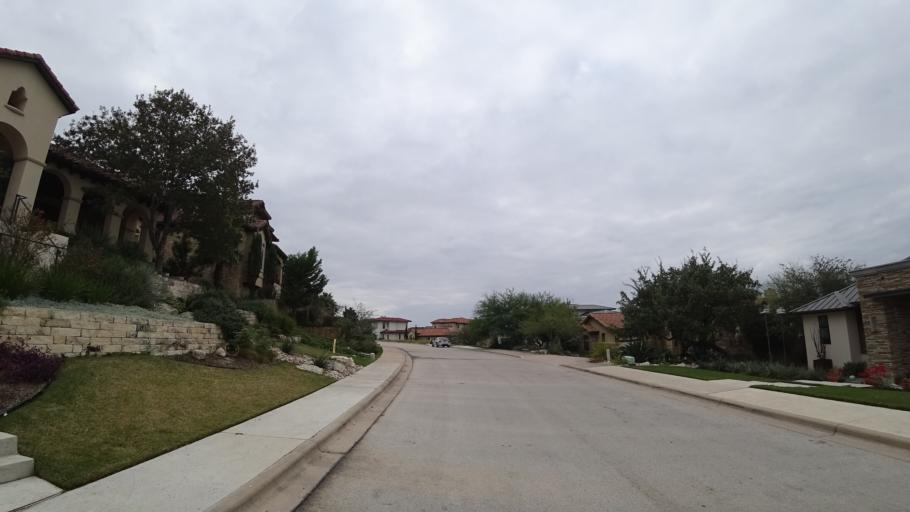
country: US
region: Texas
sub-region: Travis County
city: Bee Cave
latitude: 30.3200
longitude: -97.9175
